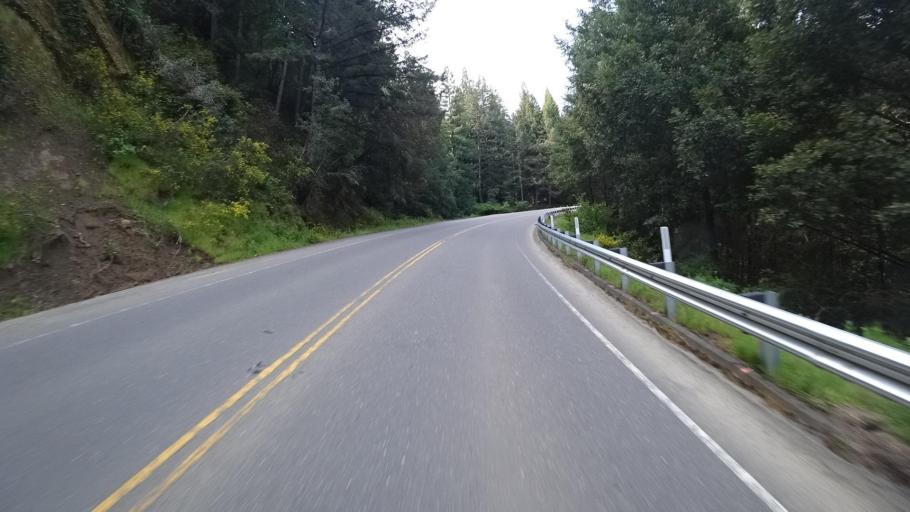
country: US
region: California
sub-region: Humboldt County
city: Redway
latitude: 40.1265
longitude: -123.8217
